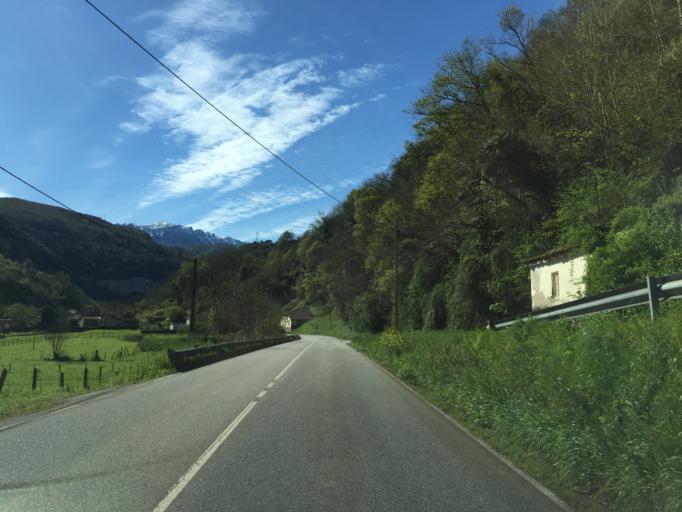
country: ES
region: Asturias
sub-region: Province of Asturias
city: Proaza
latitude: 43.3169
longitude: -5.9917
